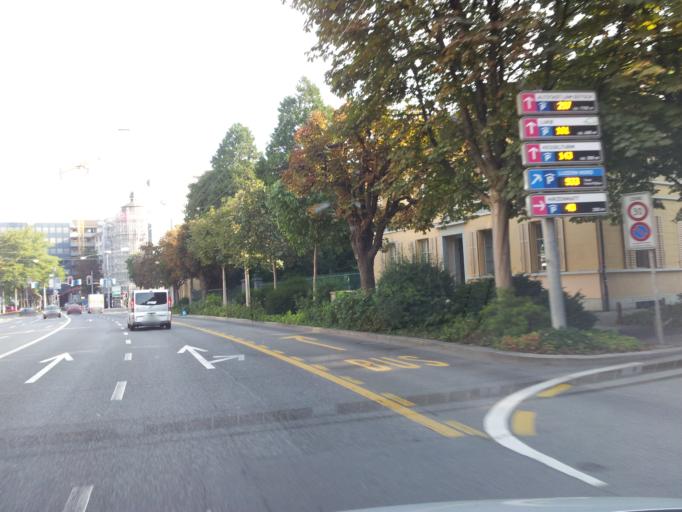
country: CH
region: Lucerne
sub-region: Lucerne-Stadt District
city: Luzern
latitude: 47.0466
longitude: 8.3042
